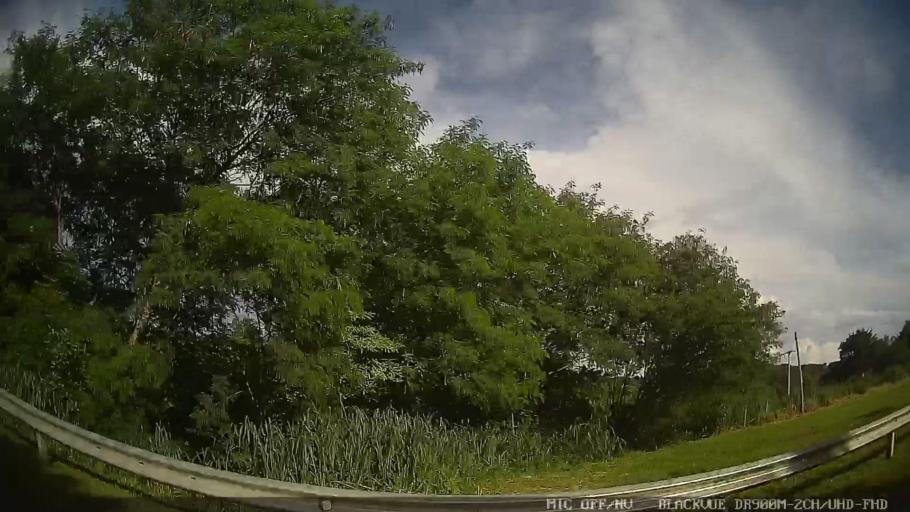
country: BR
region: Sao Paulo
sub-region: Tiete
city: Tiete
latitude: -23.1112
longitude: -47.6963
